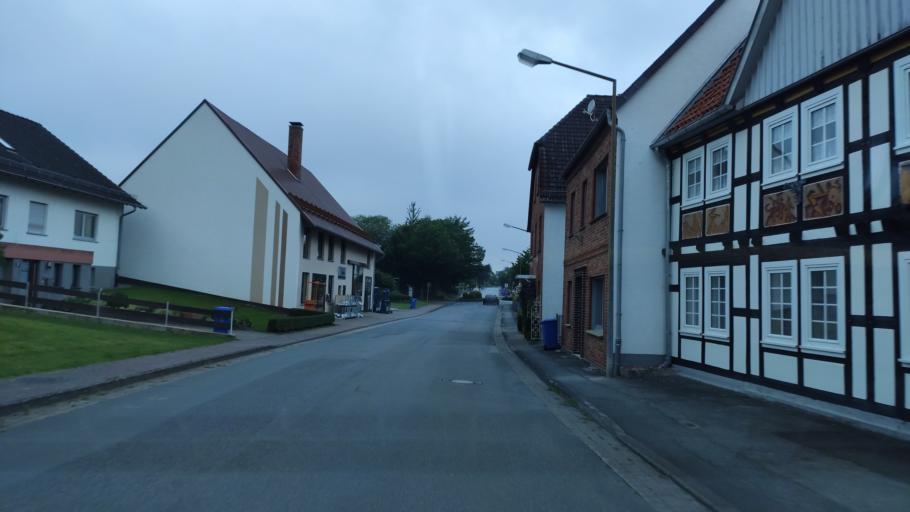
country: DE
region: North Rhine-Westphalia
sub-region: Regierungsbezirk Detmold
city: Schieder-Schwalenberg
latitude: 51.8408
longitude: 9.1715
